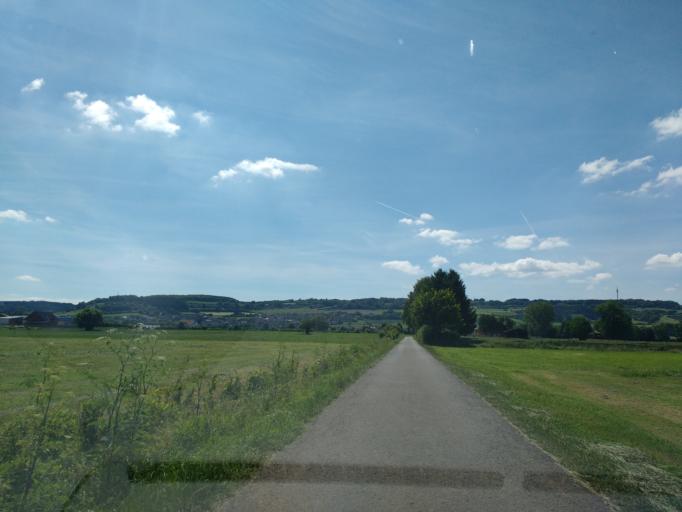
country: DE
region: Lower Saxony
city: Bad Pyrmont
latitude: 51.9728
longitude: 9.2568
